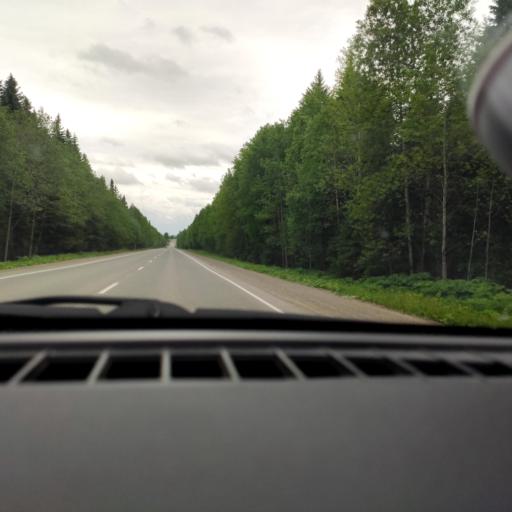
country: RU
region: Perm
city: Ust'-Kachka
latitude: 57.9087
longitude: 55.7748
